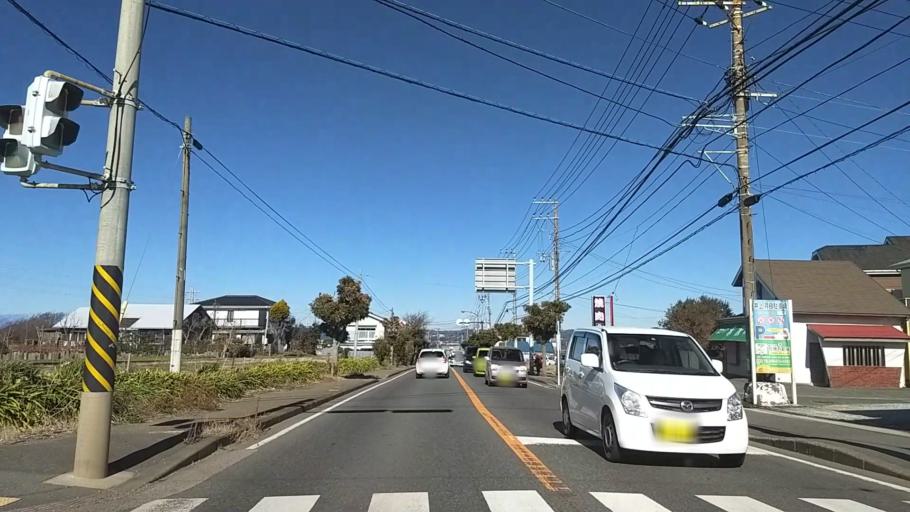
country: JP
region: Kanagawa
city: Miura
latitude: 35.1747
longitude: 139.6345
